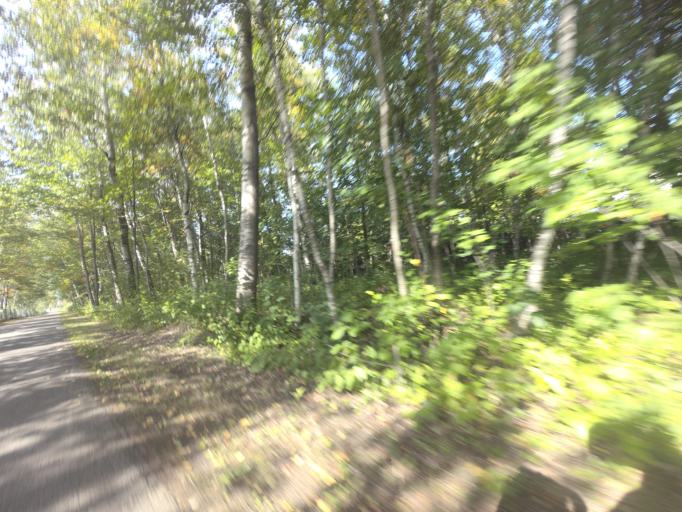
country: CA
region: Quebec
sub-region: Laurentides
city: Blainville
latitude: 45.7063
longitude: -73.9110
